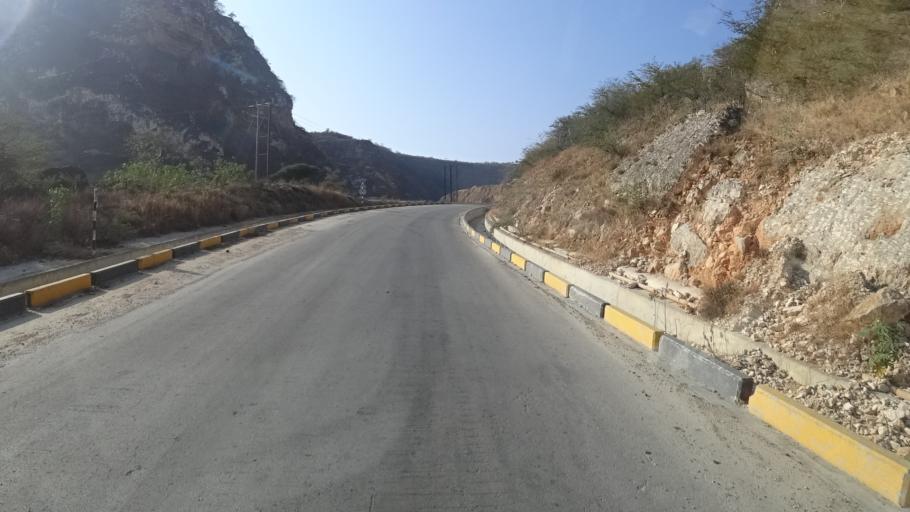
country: YE
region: Al Mahrah
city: Hawf
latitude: 16.7397
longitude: 53.2266
